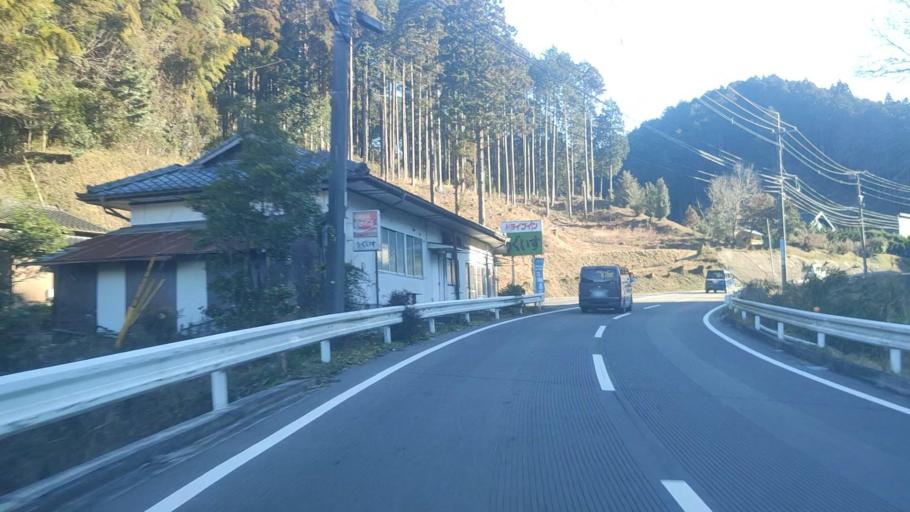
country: JP
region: Saga Prefecture
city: Kanzakimachi-kanzaki
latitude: 33.4204
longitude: 130.2791
